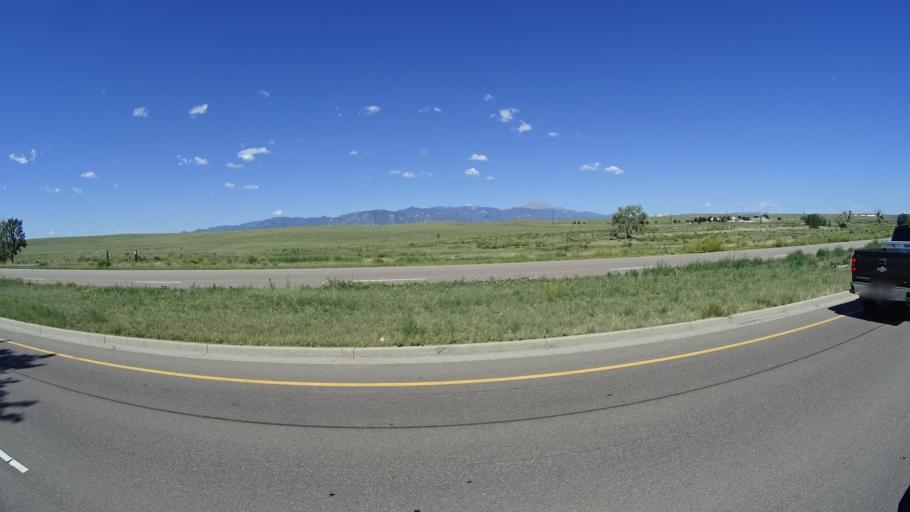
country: US
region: Colorado
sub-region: El Paso County
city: Security-Widefield
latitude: 38.7592
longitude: -104.6596
